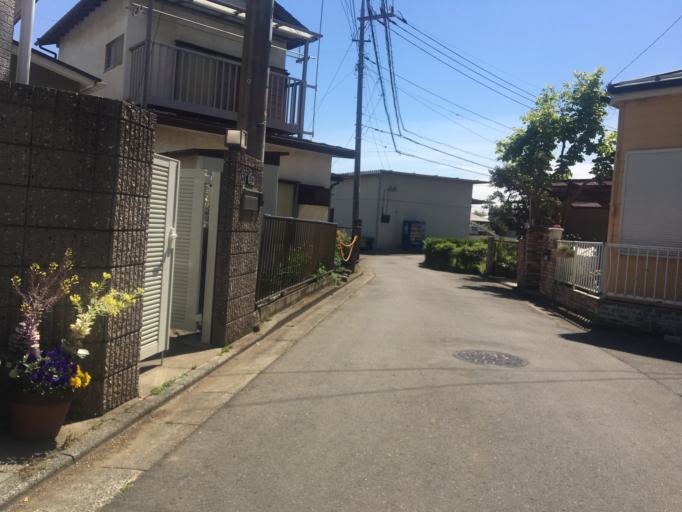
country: JP
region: Saitama
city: Shiki
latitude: 35.8392
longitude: 139.5589
